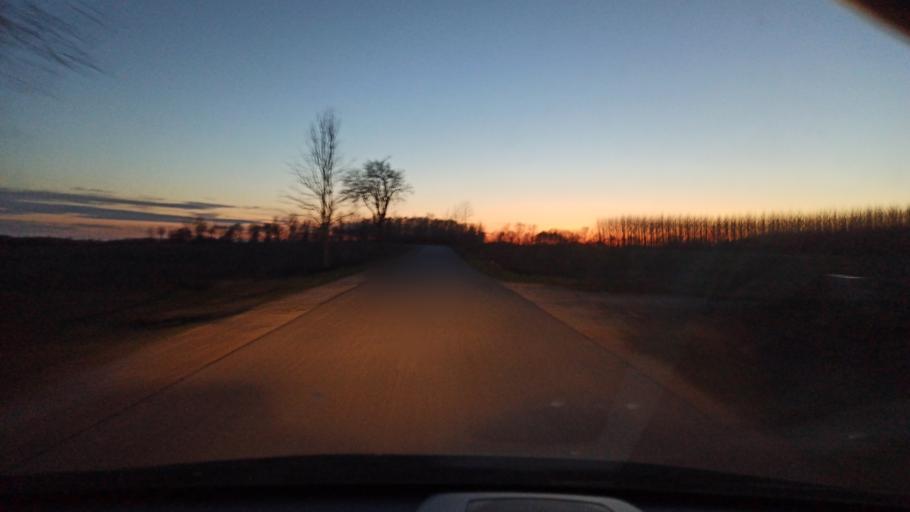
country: PL
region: Warmian-Masurian Voivodeship
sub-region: Powiat elblaski
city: Gronowo Gorne
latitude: 54.1799
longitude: 19.5300
